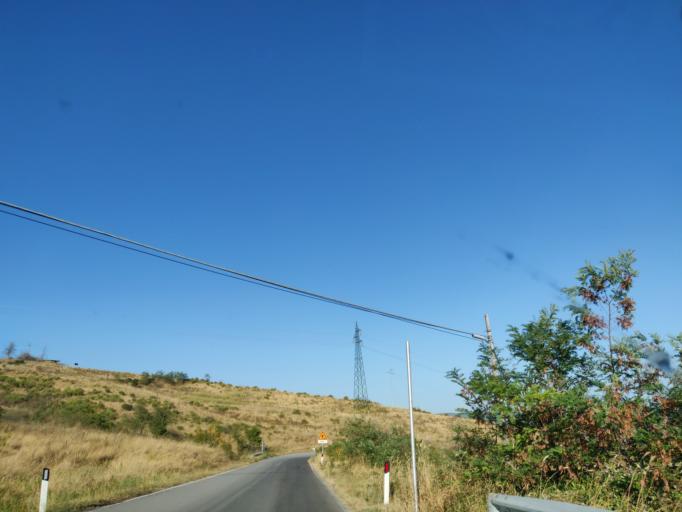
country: IT
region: Tuscany
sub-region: Provincia di Siena
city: Piancastagnaio
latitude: 42.8405
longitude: 11.7004
